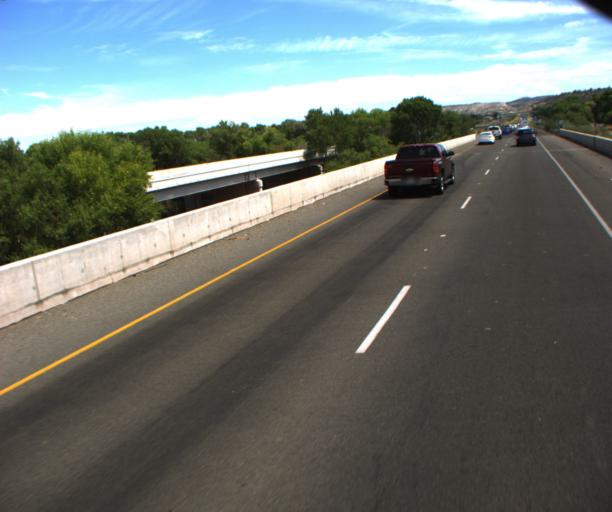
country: US
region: Arizona
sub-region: Yavapai County
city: Camp Verde
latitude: 34.5865
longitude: -111.8793
